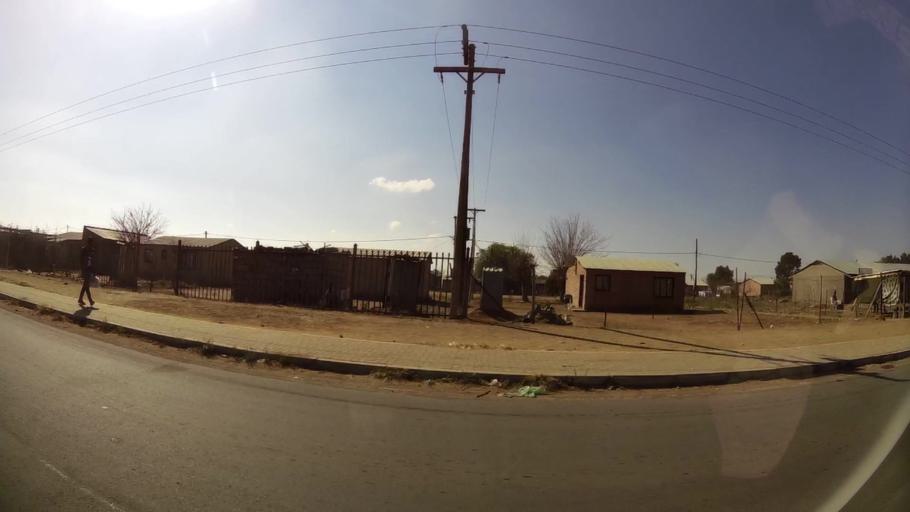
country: ZA
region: Orange Free State
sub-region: Mangaung Metropolitan Municipality
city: Bloemfontein
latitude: -29.1600
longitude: 26.2778
